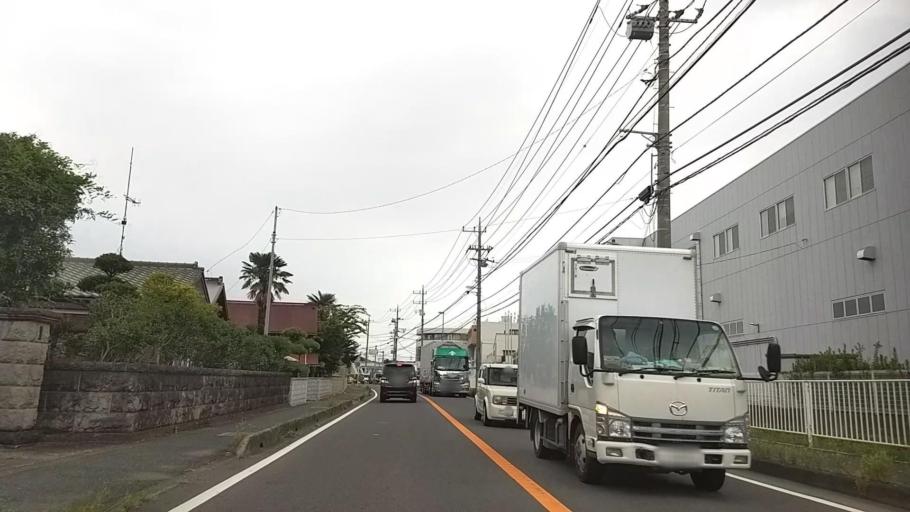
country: JP
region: Kanagawa
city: Zama
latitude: 35.4613
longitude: 139.3876
